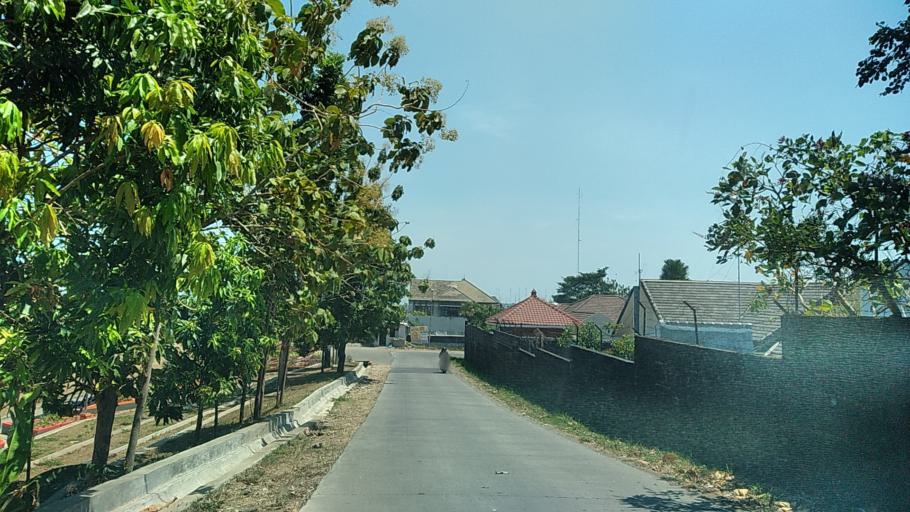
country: ID
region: Central Java
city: Ungaran
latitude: -7.0880
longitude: 110.4164
